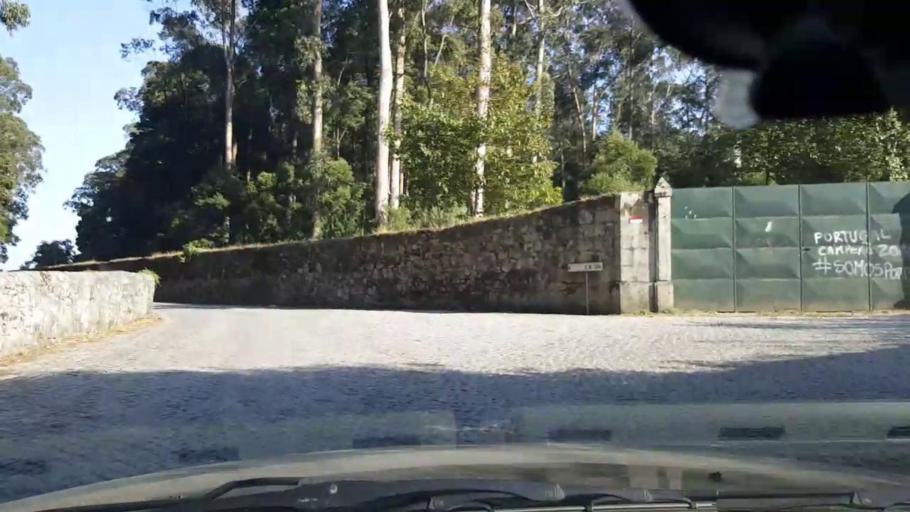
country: PT
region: Porto
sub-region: Vila do Conde
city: Arvore
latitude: 41.3466
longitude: -8.6900
